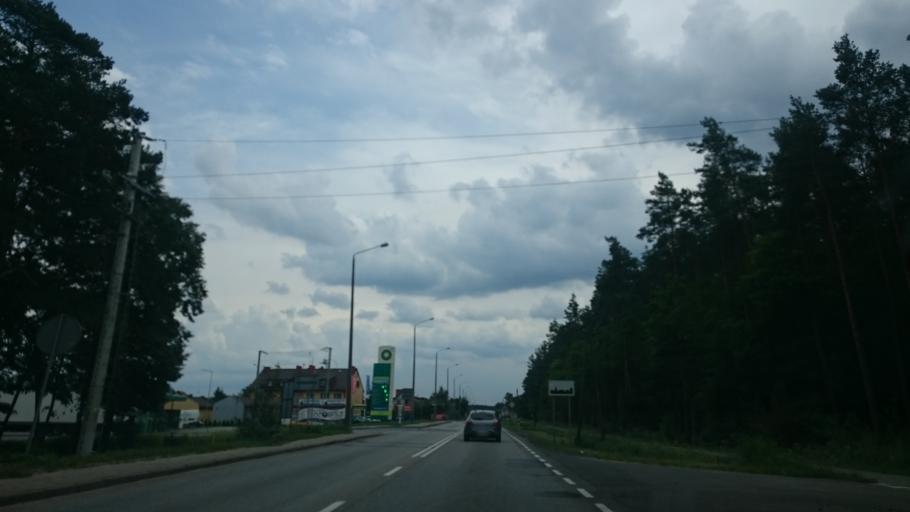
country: PL
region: Kujawsko-Pomorskie
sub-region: Powiat tucholski
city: Tuchola
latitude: 53.5730
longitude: 17.8854
